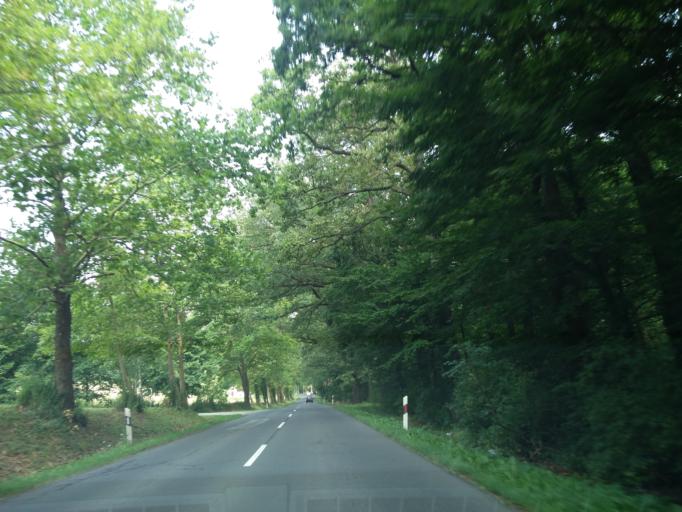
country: HU
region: Zala
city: Zalaegerszeg
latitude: 46.8098
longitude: 16.8245
